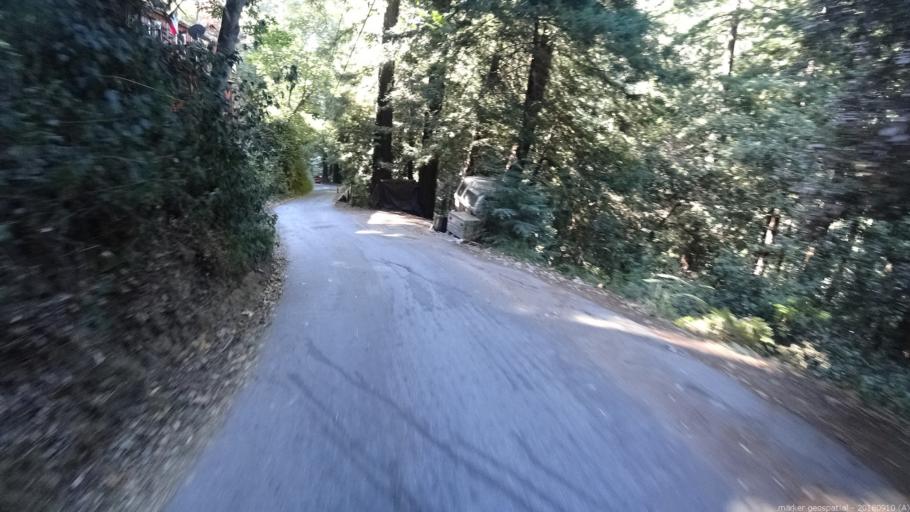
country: US
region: California
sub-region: Monterey County
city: Carmel Valley Village
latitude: 36.3966
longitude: -121.8797
